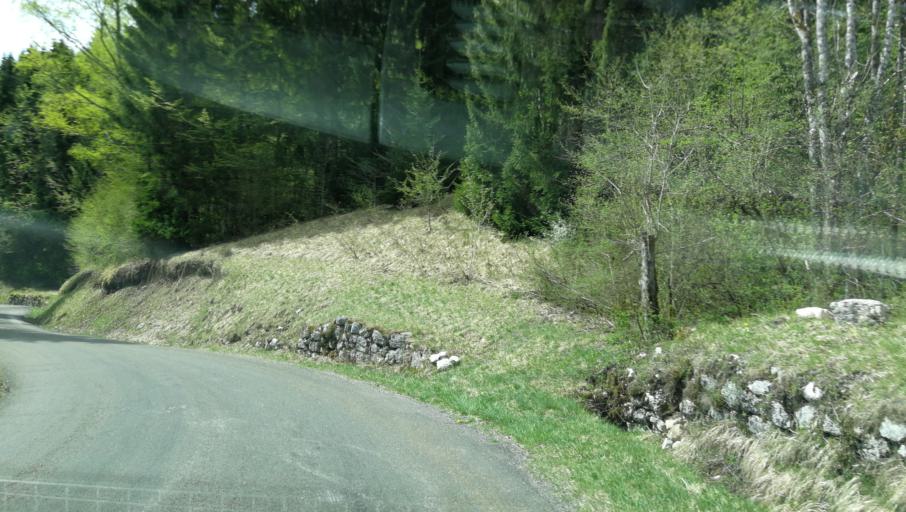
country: FR
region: Rhone-Alpes
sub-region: Departement de l'Ain
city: Oyonnax
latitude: 46.2233
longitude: 5.7437
